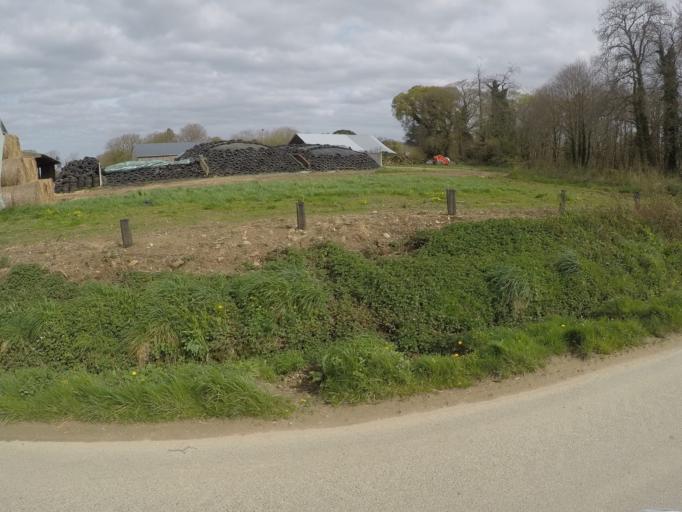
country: FR
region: Brittany
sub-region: Departement des Cotes-d'Armor
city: Plouha
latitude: 48.7119
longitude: -2.9550
